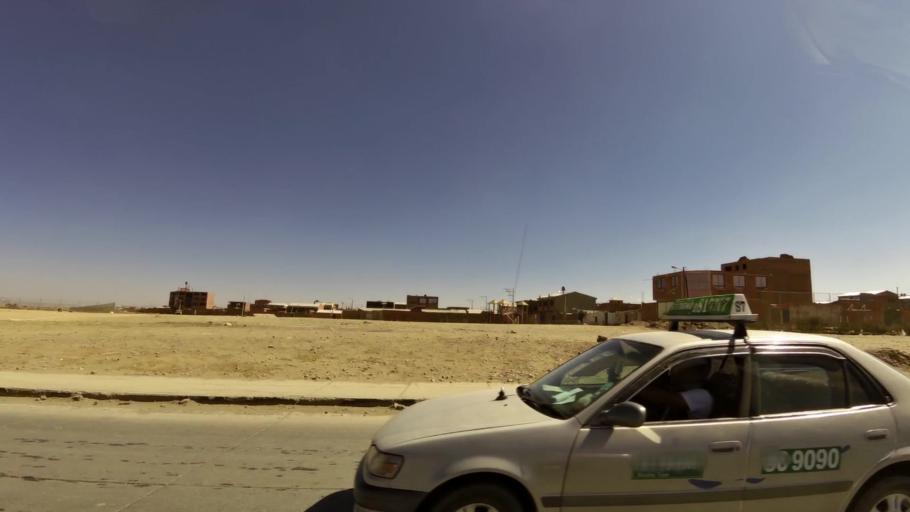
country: BO
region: La Paz
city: La Paz
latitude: -16.5120
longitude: -68.2160
